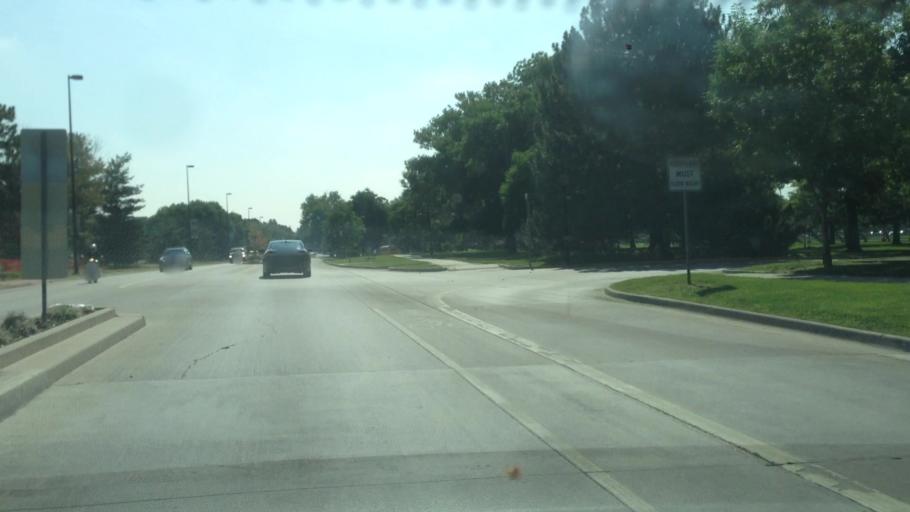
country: US
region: Colorado
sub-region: Denver County
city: Denver
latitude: 39.7512
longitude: -104.9461
